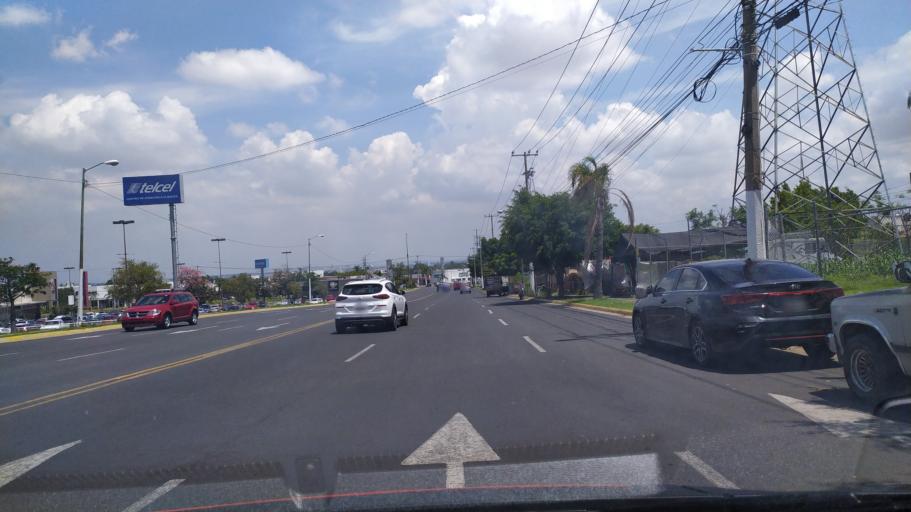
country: MX
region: Jalisco
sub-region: Zapopan
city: Zapopan
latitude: 20.7551
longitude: -103.3858
